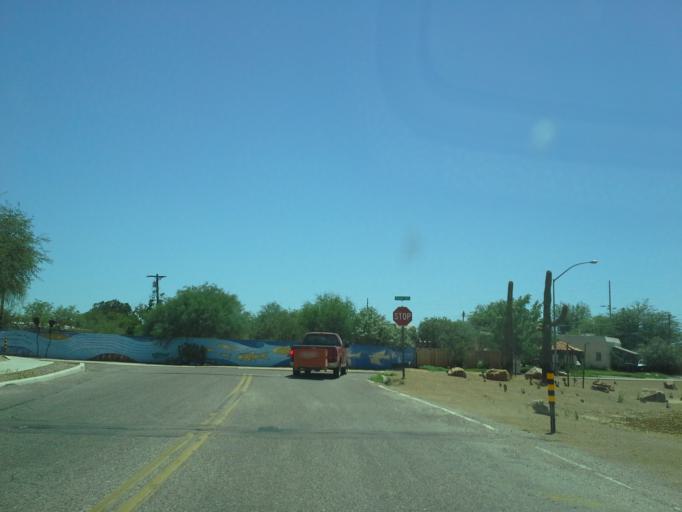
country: US
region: Arizona
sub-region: Pima County
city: Flowing Wells
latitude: 32.2809
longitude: -110.9720
